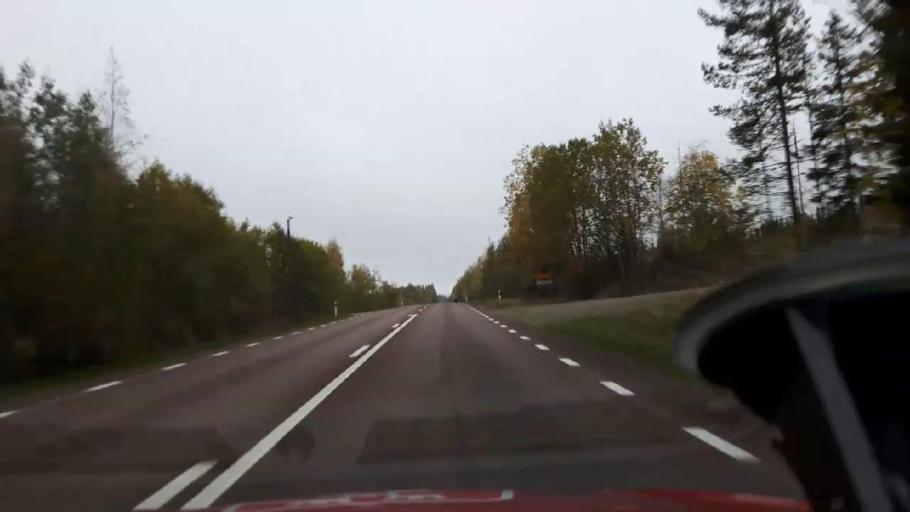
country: SE
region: Jaemtland
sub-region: Bergs Kommun
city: Hoverberg
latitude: 62.5884
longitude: 14.4342
